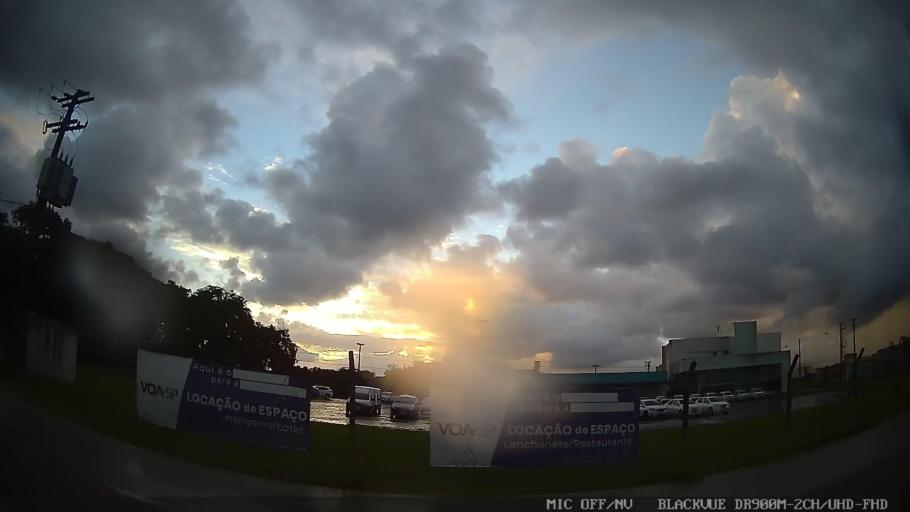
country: BR
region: Sao Paulo
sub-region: Itanhaem
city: Itanhaem
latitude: -24.1663
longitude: -46.7842
